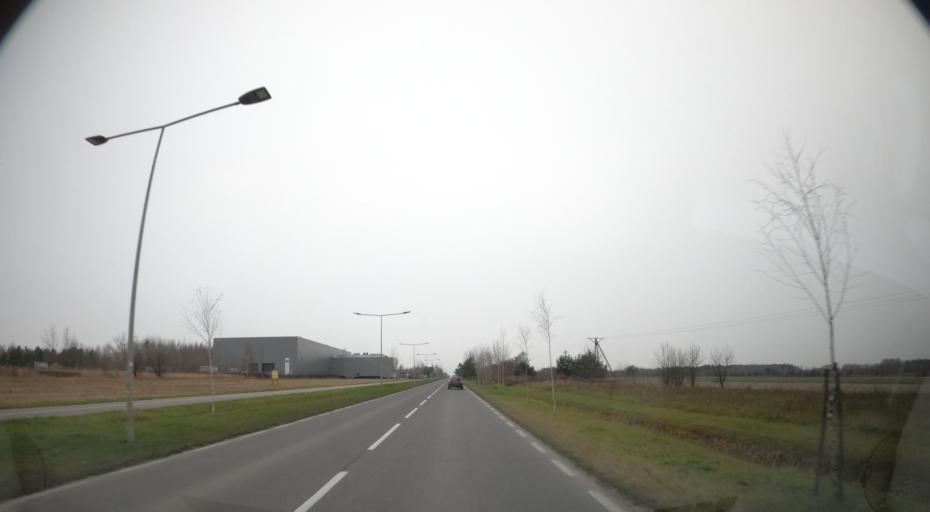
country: PL
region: Masovian Voivodeship
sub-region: Radom
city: Radom
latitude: 51.4488
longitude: 21.1931
